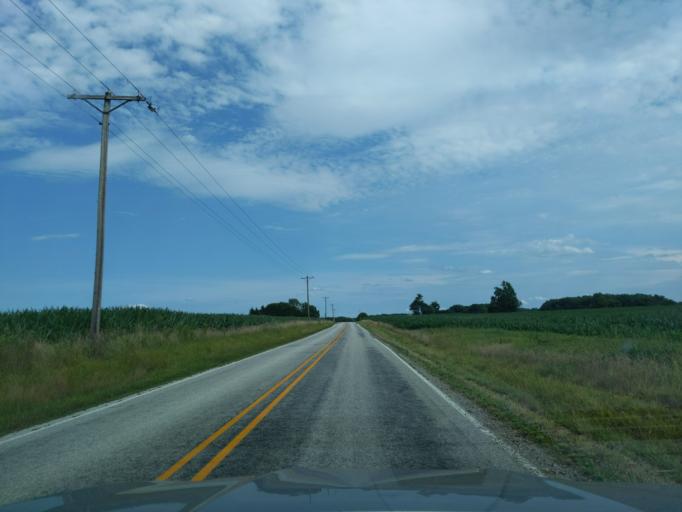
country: US
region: Indiana
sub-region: Ripley County
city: Osgood
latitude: 39.1969
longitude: -85.2392
